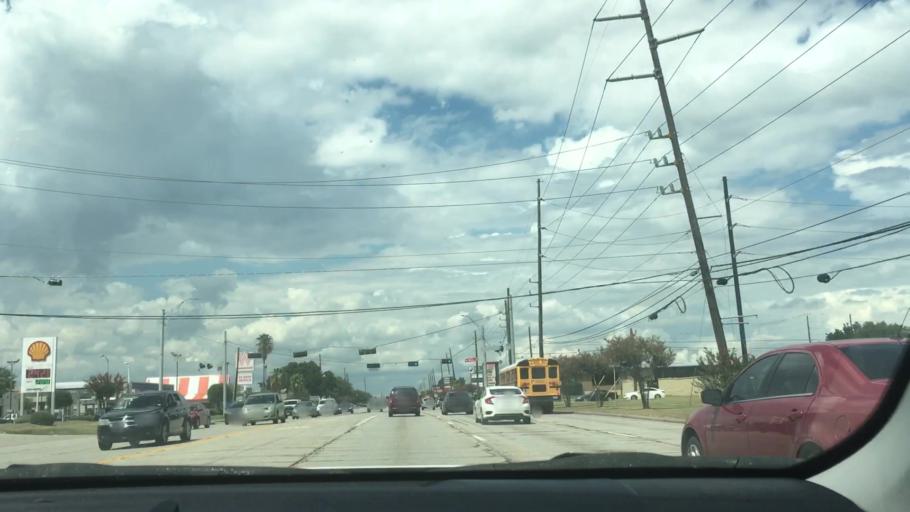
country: US
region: Texas
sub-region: Fort Bend County
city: Stafford
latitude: 29.6317
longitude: -95.5650
